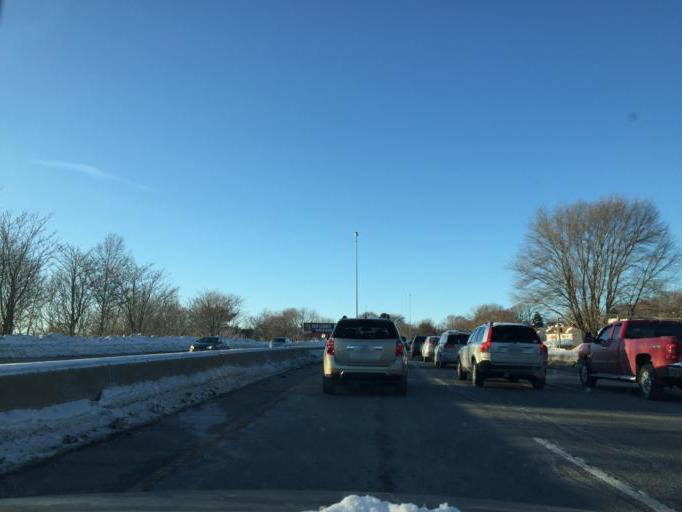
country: US
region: Massachusetts
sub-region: Suffolk County
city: Revere
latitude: 42.4111
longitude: -71.0292
